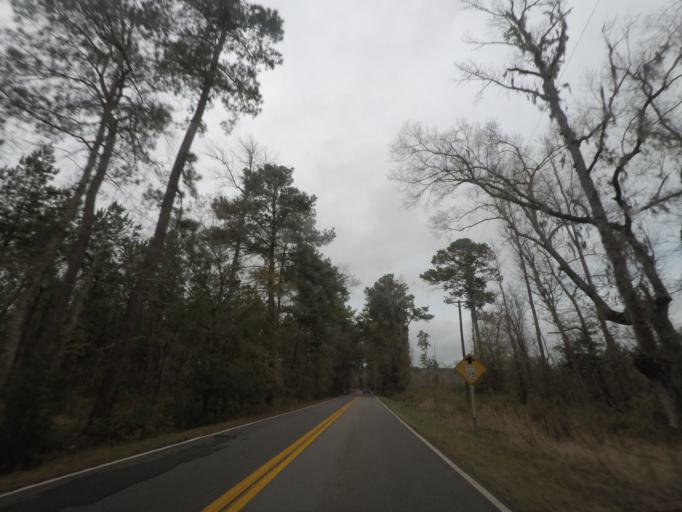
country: US
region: South Carolina
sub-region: Colleton County
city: Walterboro
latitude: 32.9326
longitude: -80.5388
